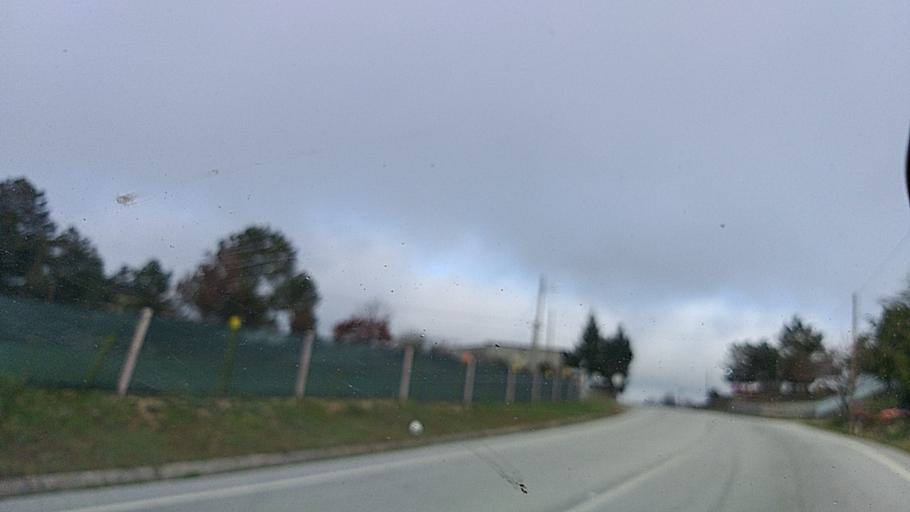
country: PT
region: Guarda
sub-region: Aguiar da Beira
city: Aguiar da Beira
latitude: 40.7387
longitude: -7.4941
